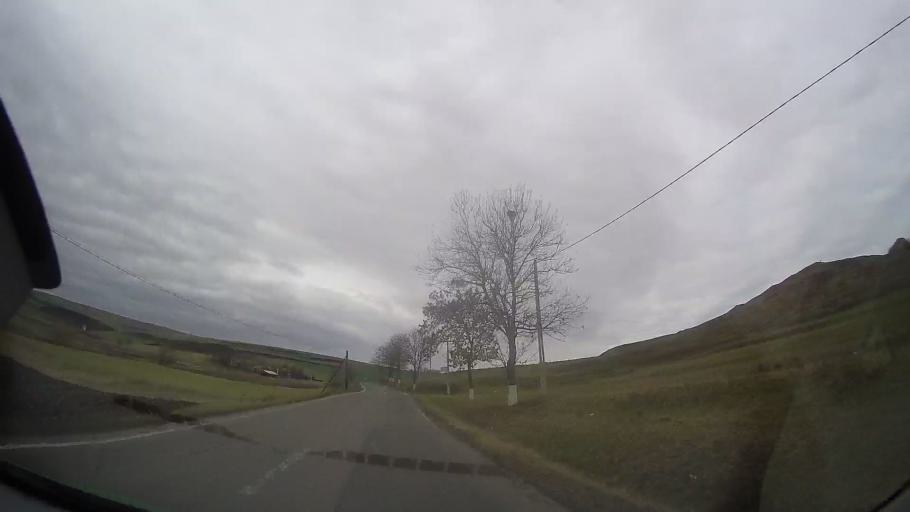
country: RO
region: Bistrita-Nasaud
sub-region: Comuna Urmenis
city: Urmenis
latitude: 46.7610
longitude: 24.3872
